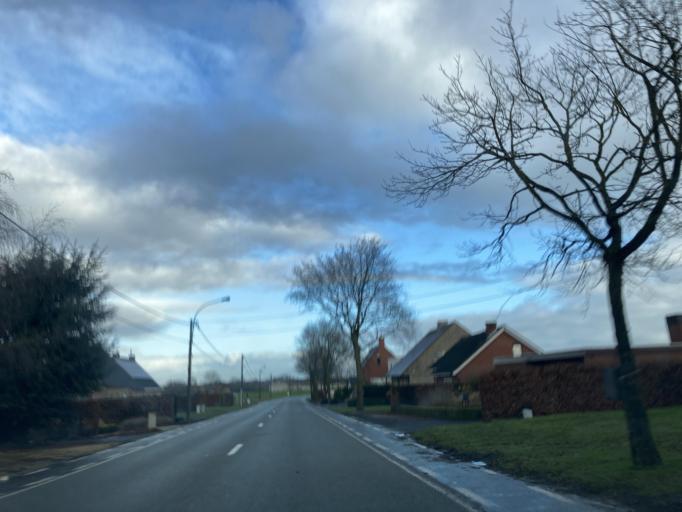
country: BE
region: Flanders
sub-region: Provincie West-Vlaanderen
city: Tielt
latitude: 51.0198
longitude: 3.3324
